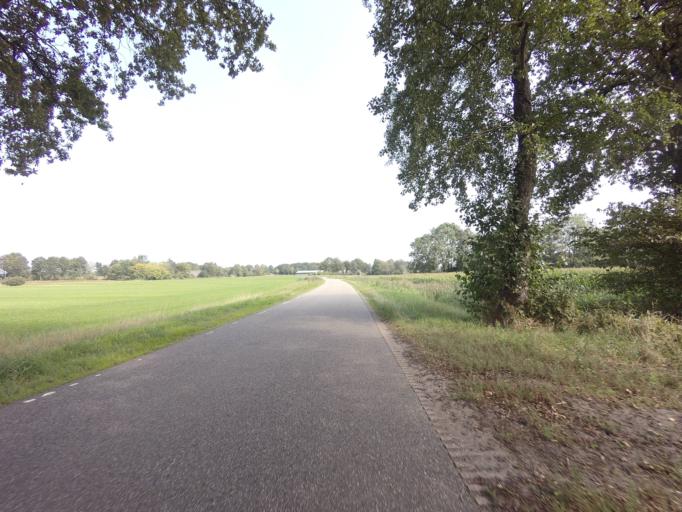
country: NL
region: Drenthe
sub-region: Gemeente Assen
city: Assen
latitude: 52.9625
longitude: 6.6139
